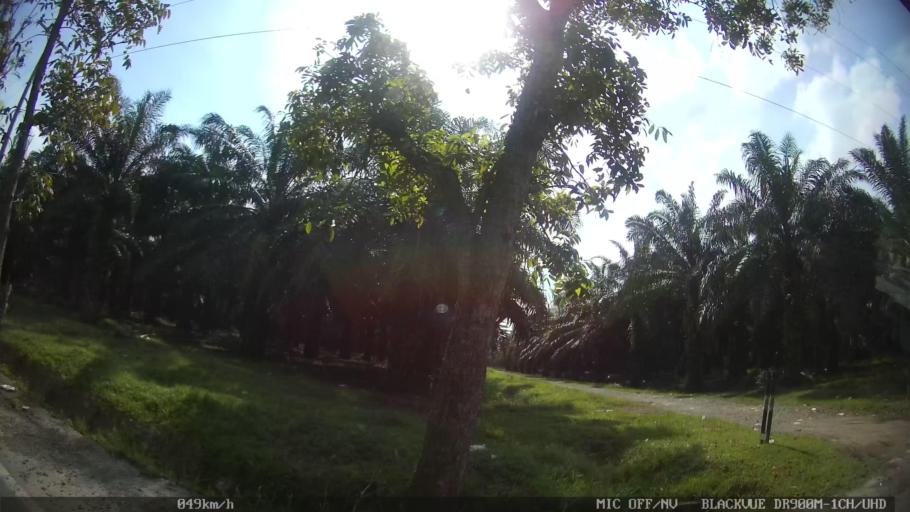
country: ID
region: North Sumatra
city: Binjai
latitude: 3.6413
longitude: 98.5351
